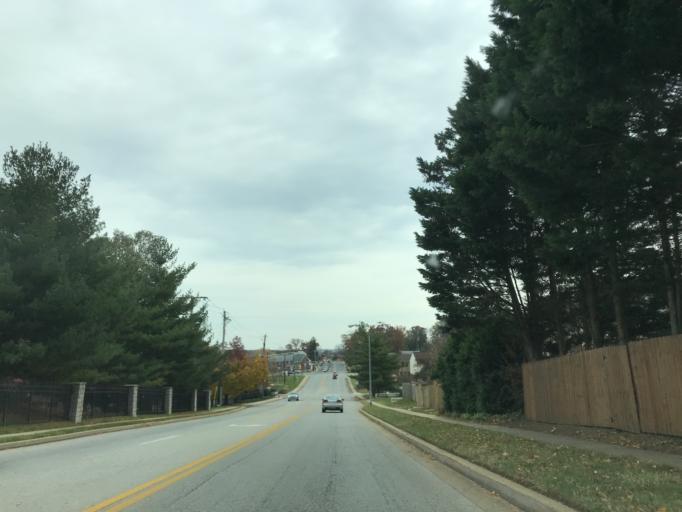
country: US
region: Maryland
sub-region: Baltimore County
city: Charlestown
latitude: 39.2663
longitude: -76.7026
